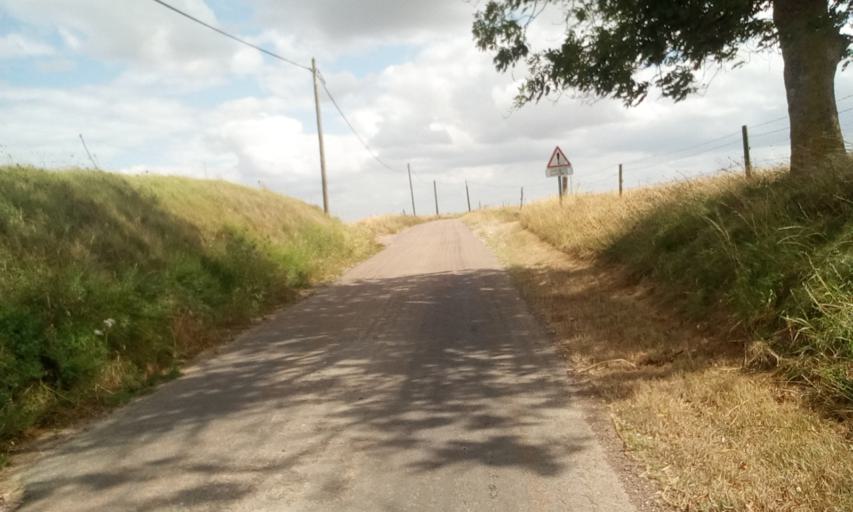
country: FR
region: Lower Normandy
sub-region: Departement du Calvados
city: Ver-sur-Mer
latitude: 49.3288
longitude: -0.5256
